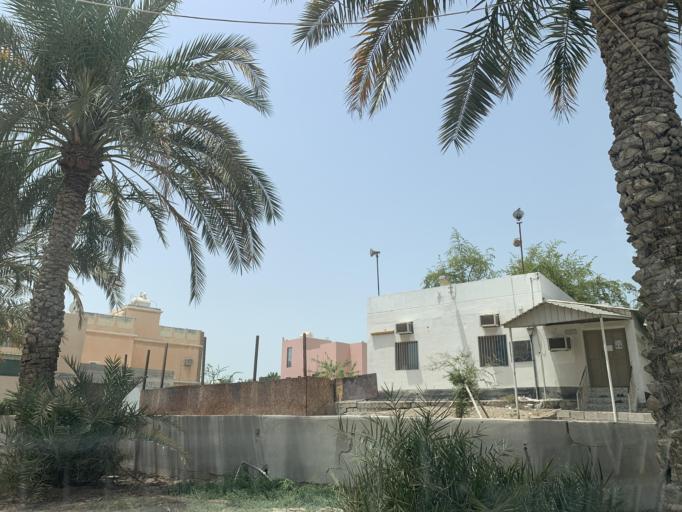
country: BH
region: Northern
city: Sitrah
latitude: 26.1509
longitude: 50.5861
